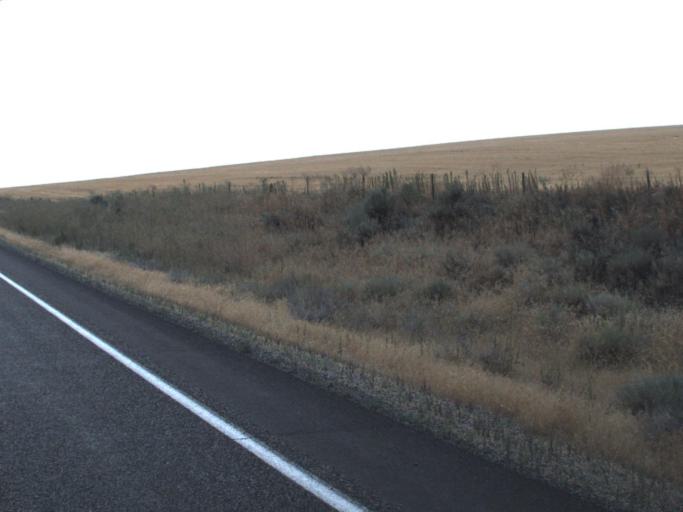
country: US
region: Washington
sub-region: Benton County
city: Prosser
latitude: 46.1968
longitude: -119.7058
